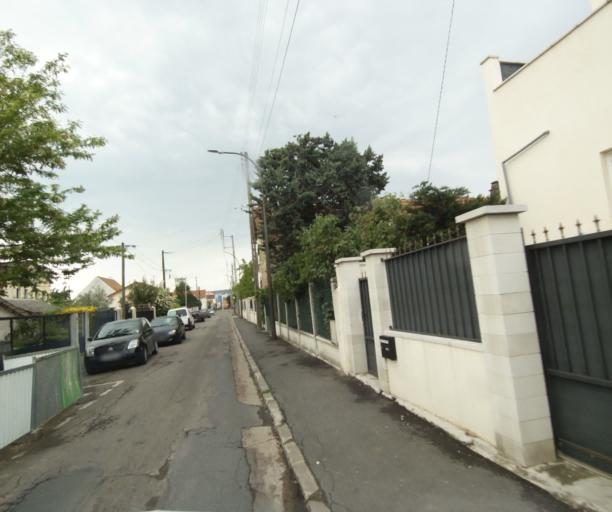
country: FR
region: Ile-de-France
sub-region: Departement du Val-d'Oise
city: Bezons
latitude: 48.9442
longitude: 2.2168
